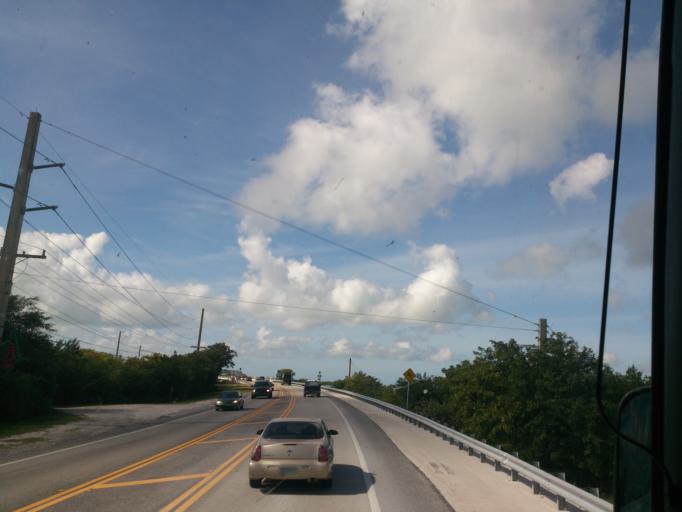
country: US
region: Florida
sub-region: Monroe County
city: Big Pine Key
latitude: 24.6699
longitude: -81.3696
